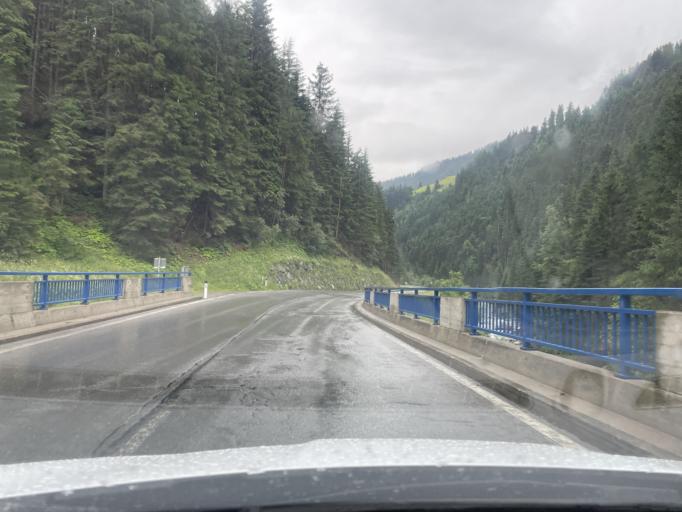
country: AT
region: Tyrol
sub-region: Politischer Bezirk Lienz
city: Ausservillgraten
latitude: 46.7808
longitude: 12.4289
